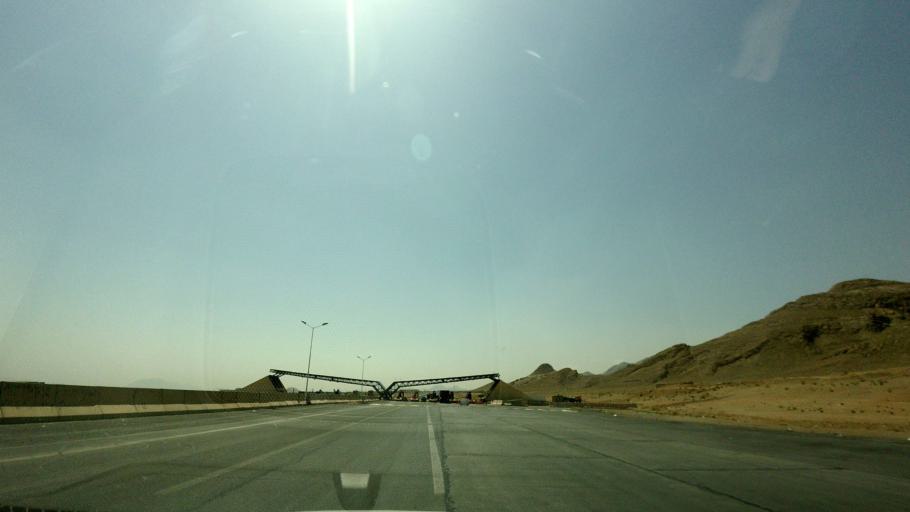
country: IR
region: Isfahan
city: Najafabad
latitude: 32.5832
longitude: 51.2871
